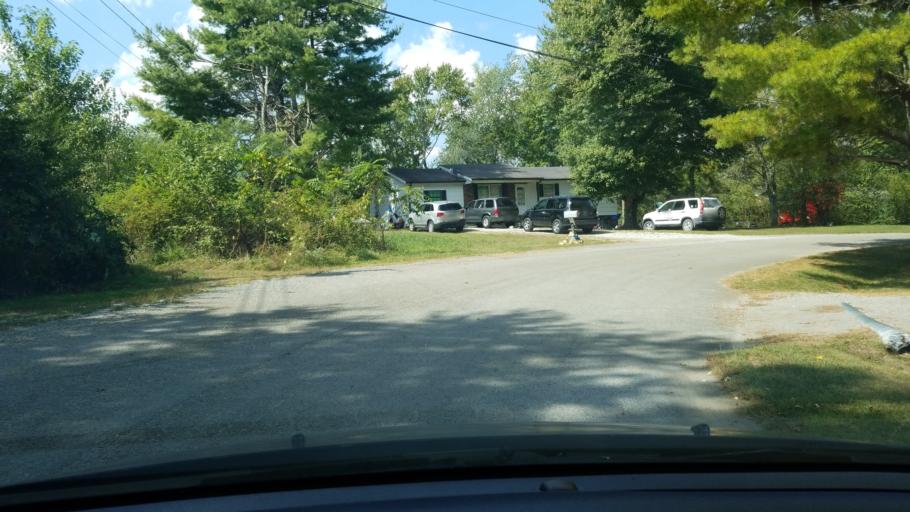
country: US
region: Tennessee
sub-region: Cumberland County
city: Crossville
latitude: 35.9590
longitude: -85.0691
